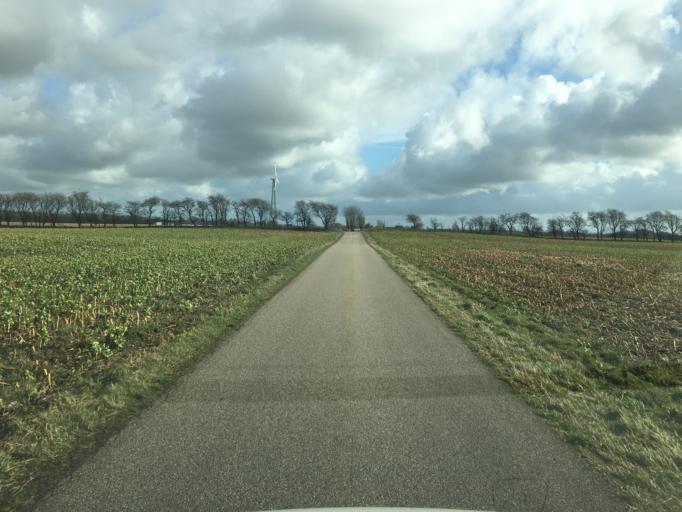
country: DK
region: South Denmark
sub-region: Aabenraa Kommune
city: Krusa
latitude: 54.9150
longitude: 9.3684
